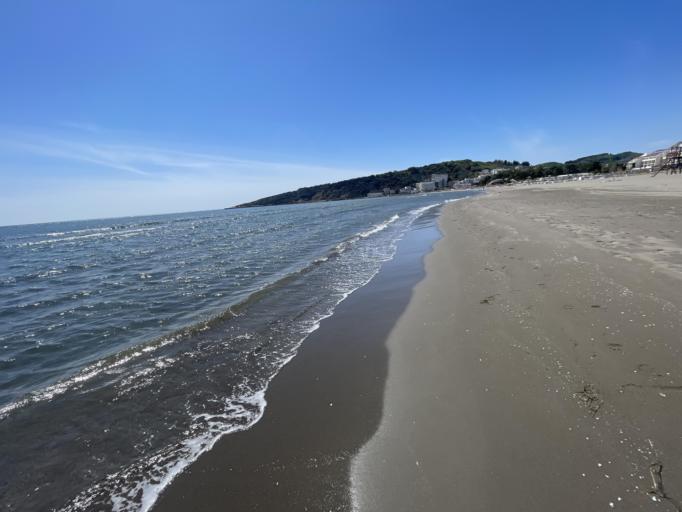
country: ME
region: Ulcinj
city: Ulcinj
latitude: 41.9085
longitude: 19.2427
